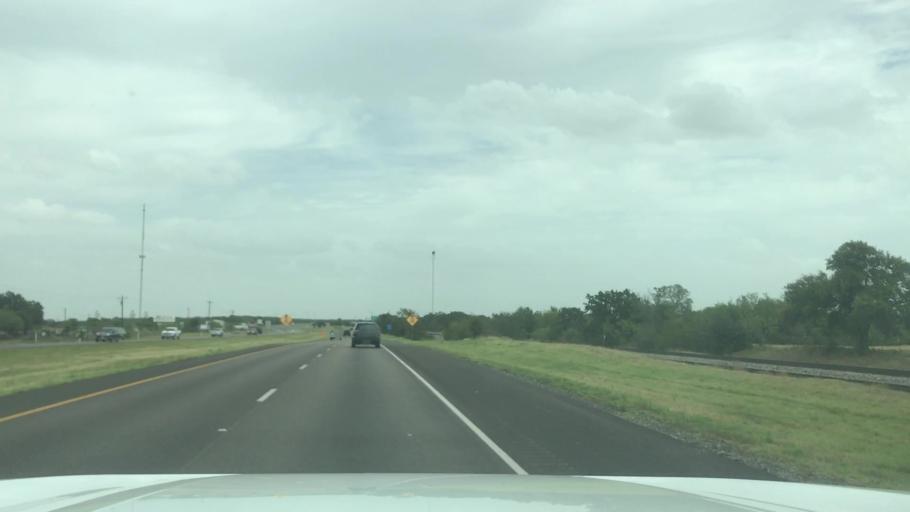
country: US
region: Texas
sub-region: McLennan County
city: Riesel
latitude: 31.5179
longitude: -96.9694
